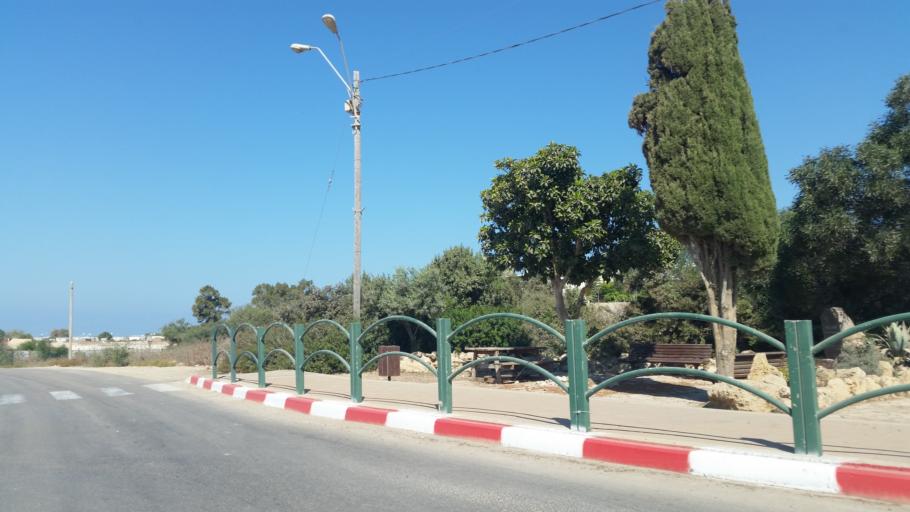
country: IL
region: Haifa
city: `Atlit
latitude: 32.6802
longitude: 34.9345
